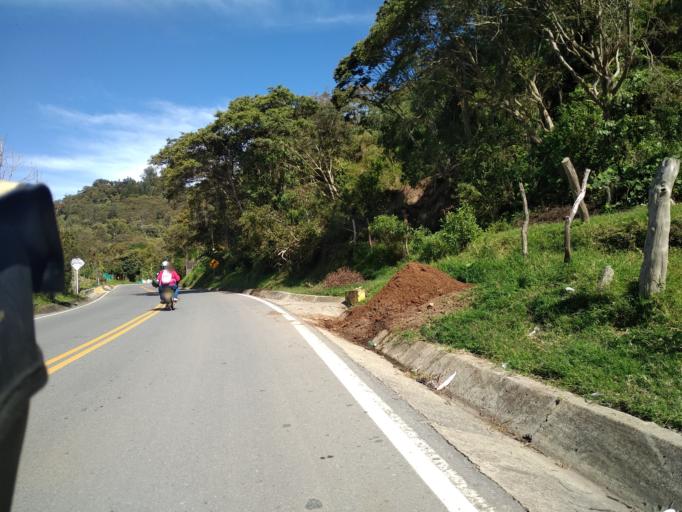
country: CO
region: Santander
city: Velez
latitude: 6.0025
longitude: -73.6806
